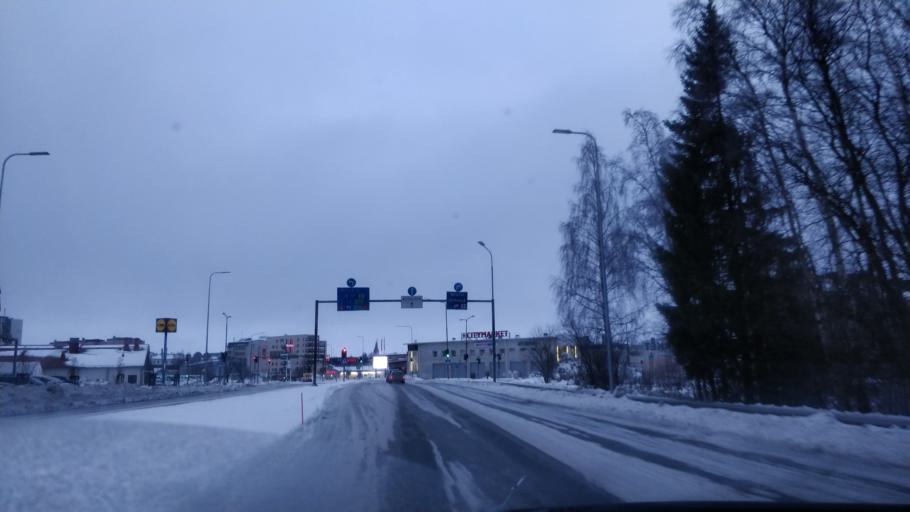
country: FI
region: Lapland
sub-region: Kemi-Tornio
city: Kemi
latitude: 65.7414
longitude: 24.5653
